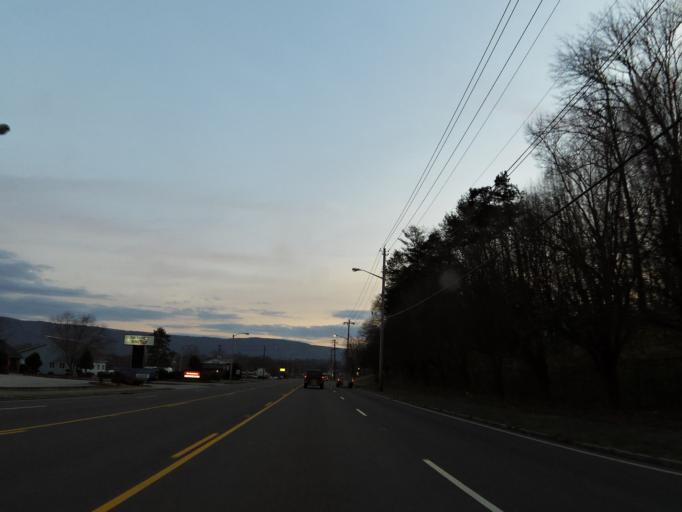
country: US
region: Tennessee
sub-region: McMinn County
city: Etowah
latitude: 35.3376
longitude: -84.5203
